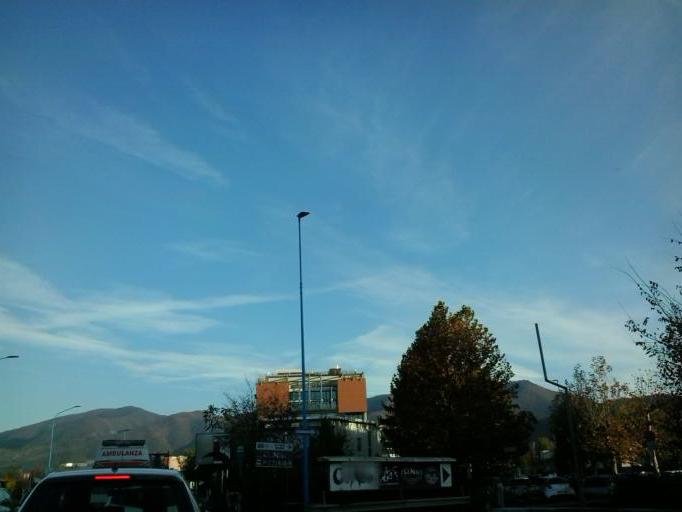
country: IT
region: Lombardy
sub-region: Provincia di Brescia
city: Collebeato
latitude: 45.5631
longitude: 10.2286
